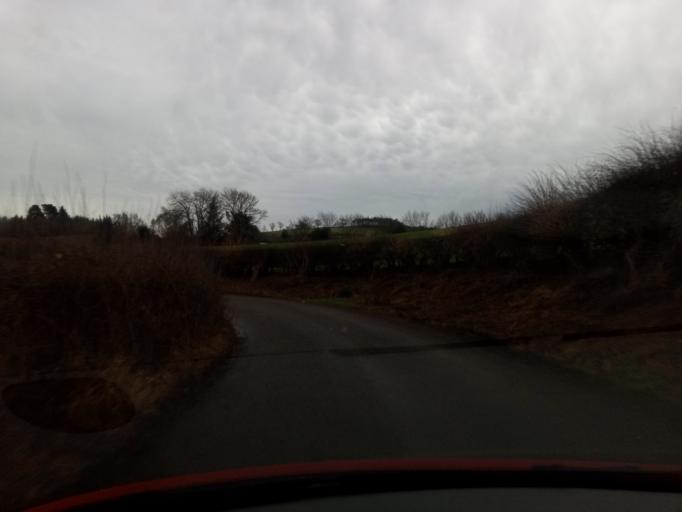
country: GB
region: England
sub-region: Northumberland
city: Wooler
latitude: 55.5496
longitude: -2.0273
